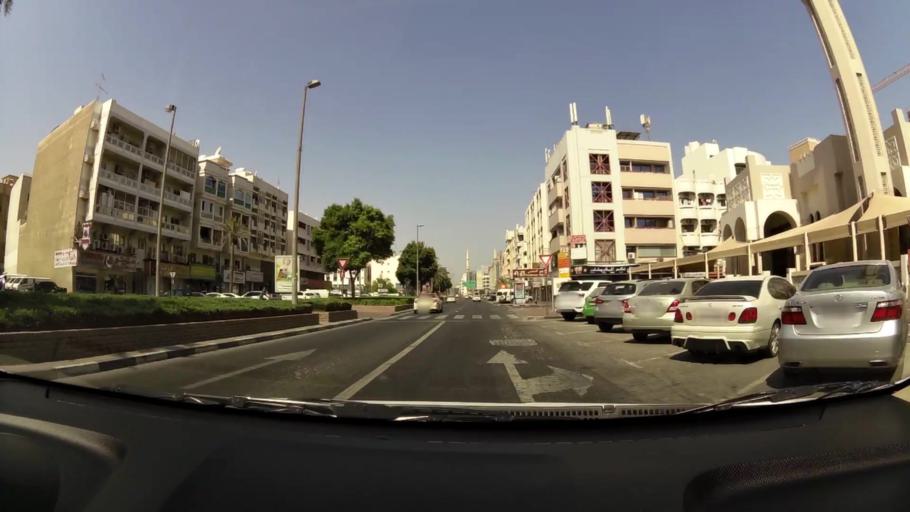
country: AE
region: Ash Shariqah
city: Sharjah
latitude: 25.2750
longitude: 55.3098
